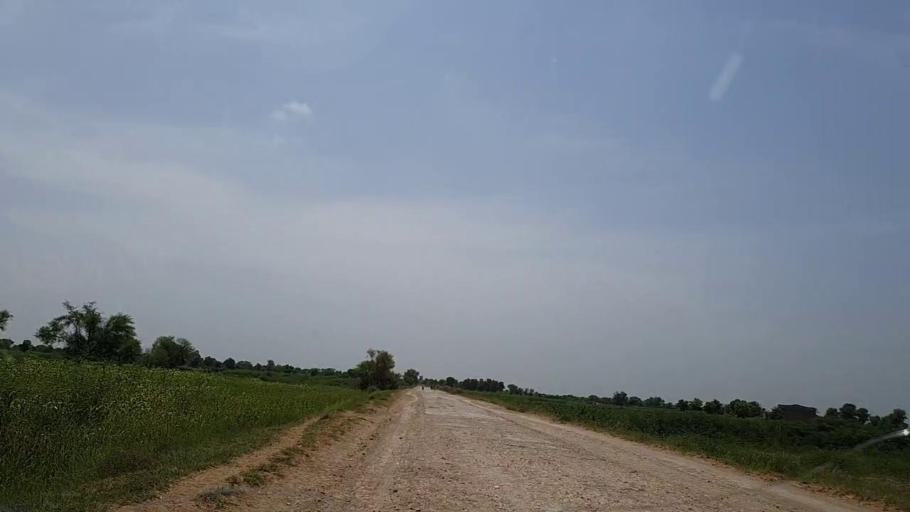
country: PK
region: Sindh
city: Khanpur
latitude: 27.8632
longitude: 69.4873
